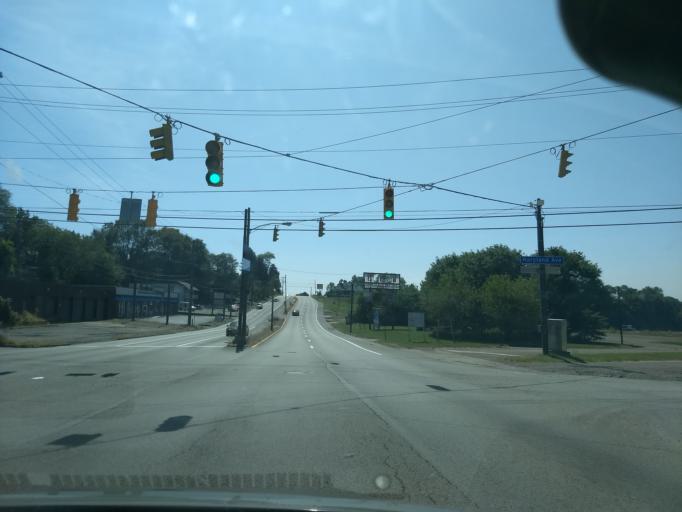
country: US
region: Pennsylvania
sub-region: Allegheny County
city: East Pittsburgh
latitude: 40.3803
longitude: -79.8285
